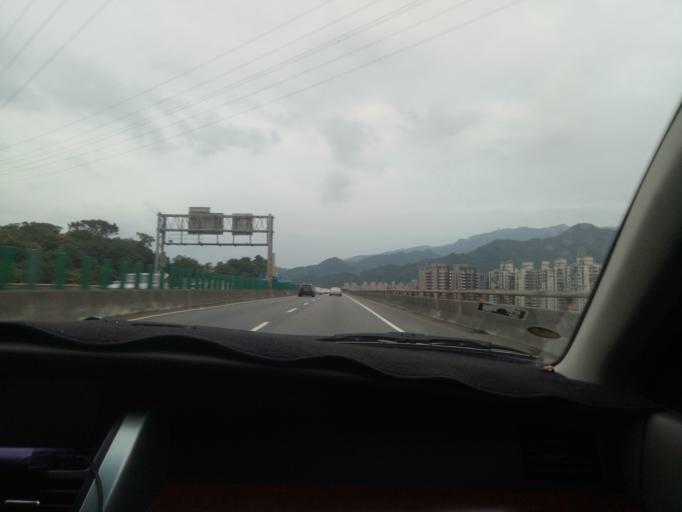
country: TW
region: Taiwan
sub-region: Keelung
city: Keelung
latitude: 25.1019
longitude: 121.7465
